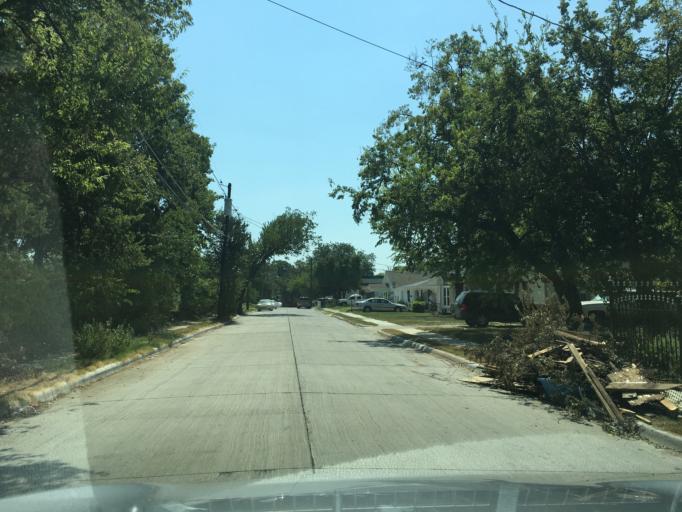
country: US
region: Texas
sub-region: Dallas County
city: Dallas
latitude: 32.7453
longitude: -96.7941
